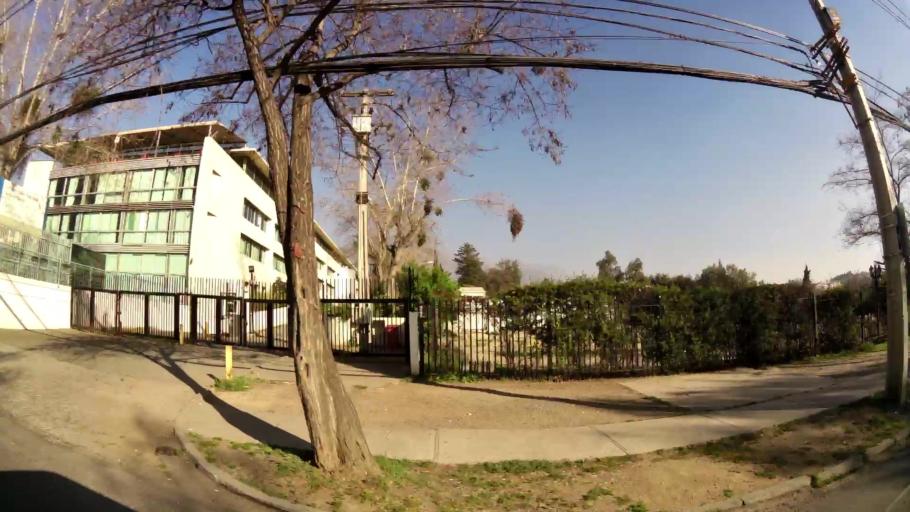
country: CL
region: Santiago Metropolitan
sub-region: Provincia de Santiago
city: Villa Presidente Frei, Nunoa, Santiago, Chile
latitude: -33.3746
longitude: -70.5067
